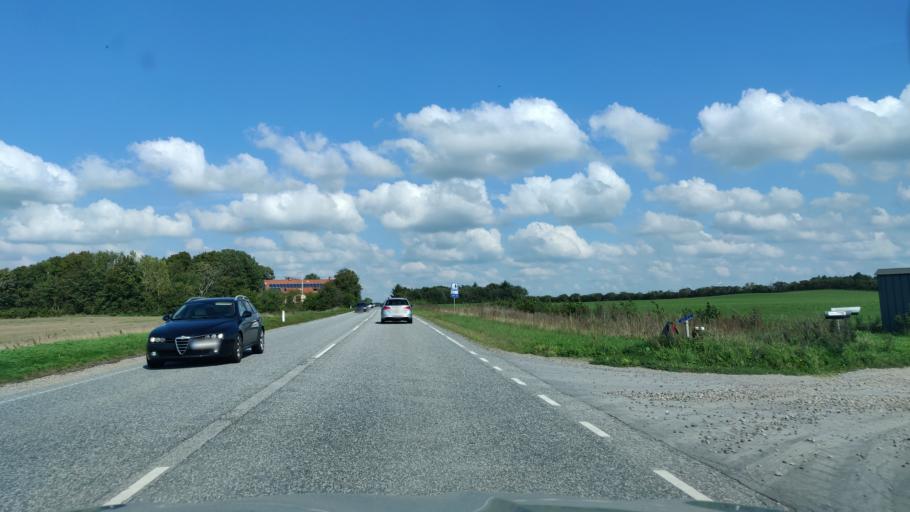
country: DK
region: North Denmark
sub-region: Vesthimmerland Kommune
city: Aars
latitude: 56.7577
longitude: 9.5521
